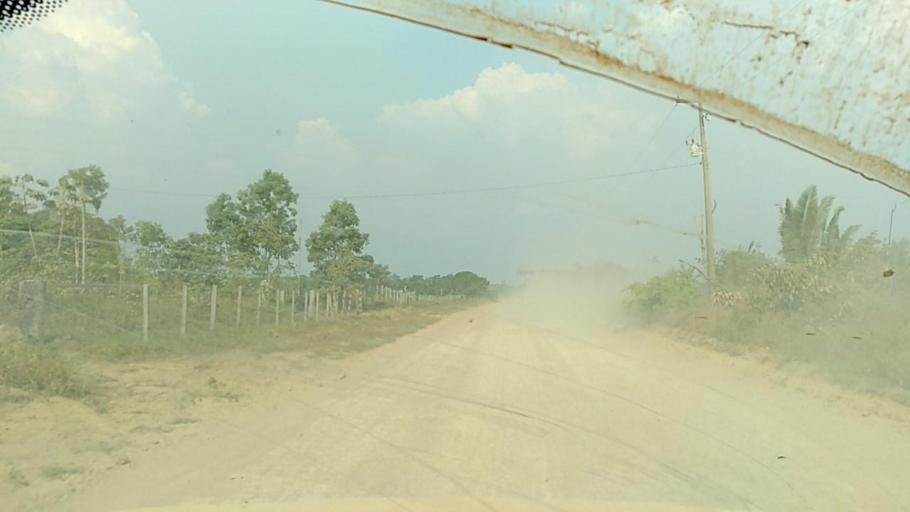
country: BR
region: Rondonia
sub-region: Porto Velho
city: Porto Velho
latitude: -8.6835
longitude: -63.1931
